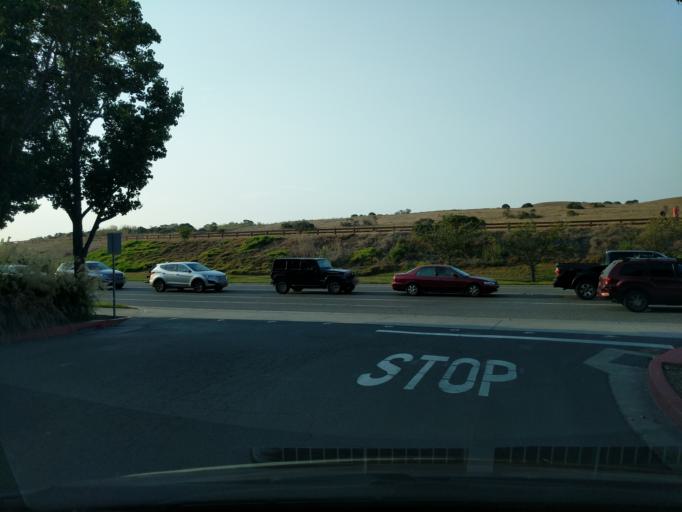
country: US
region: California
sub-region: Santa Clara County
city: Mountain View
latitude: 37.4228
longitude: -122.0833
